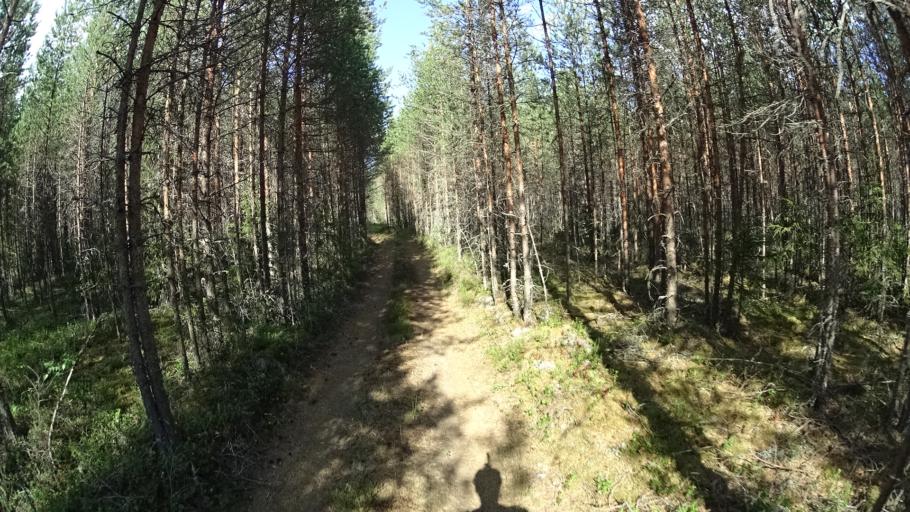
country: FI
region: Uusimaa
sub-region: Helsinki
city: Kaerkoelae
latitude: 60.7326
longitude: 24.0569
